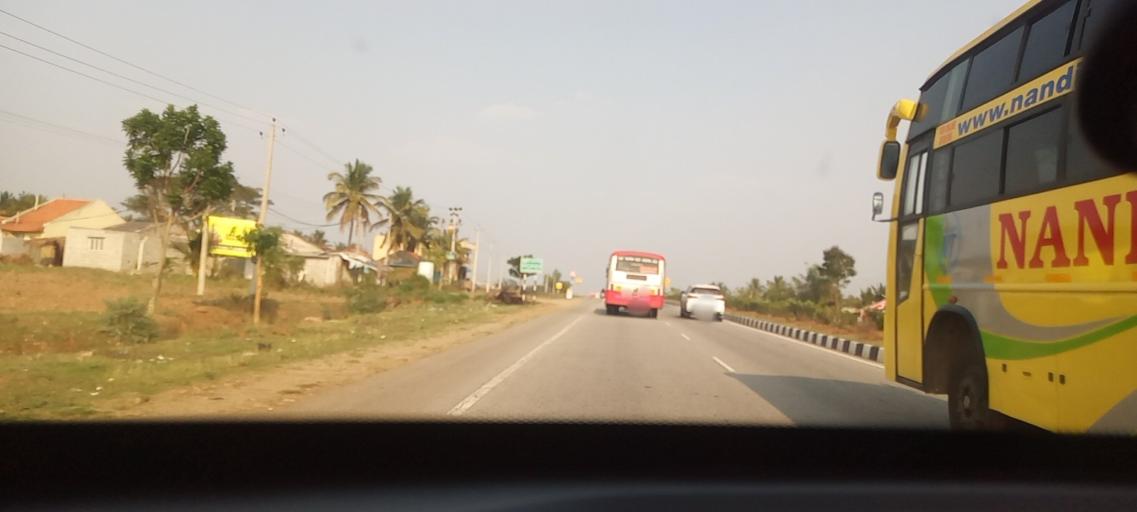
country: IN
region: Karnataka
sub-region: Hassan
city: Channarayapatna
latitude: 12.9420
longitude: 76.3532
